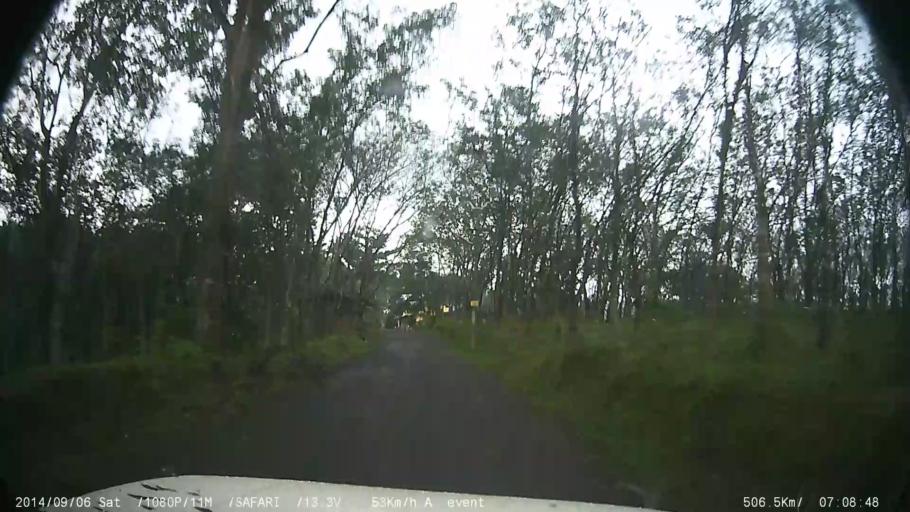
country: IN
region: Kerala
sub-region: Ernakulam
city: Piravam
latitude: 9.7946
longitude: 76.5456
